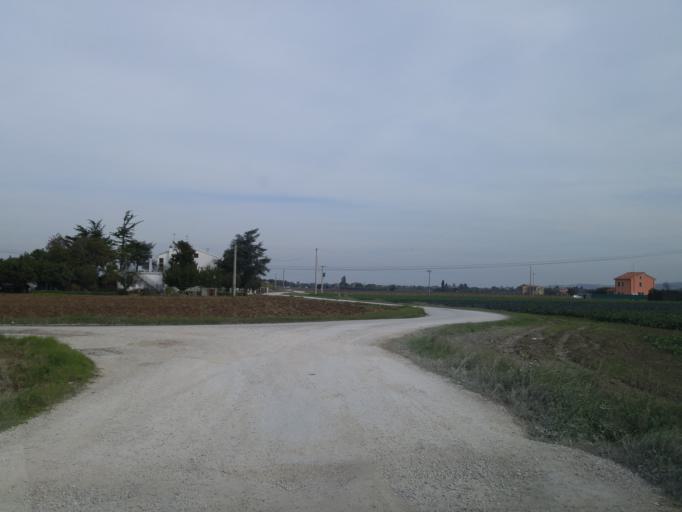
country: IT
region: The Marches
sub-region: Provincia di Pesaro e Urbino
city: Cuccurano
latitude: 43.7760
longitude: 12.9675
